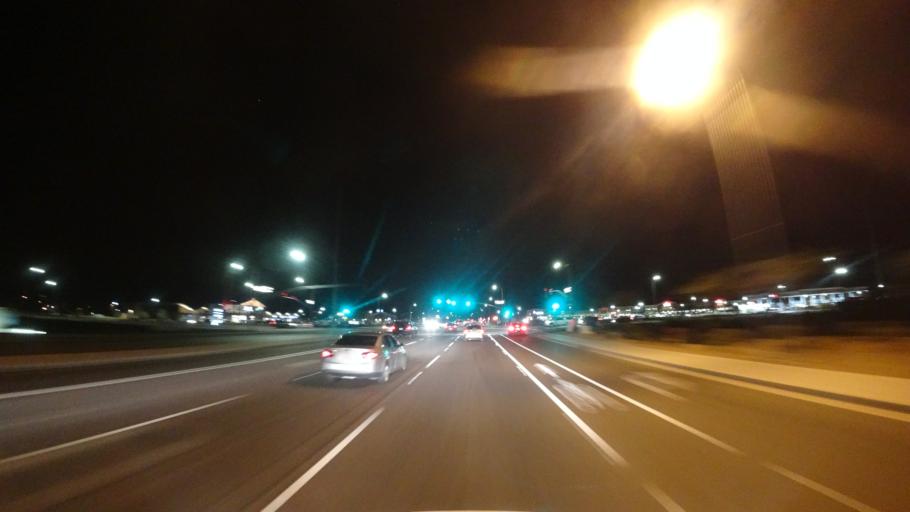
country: US
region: Arizona
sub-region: Maricopa County
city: Chandler
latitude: 33.2490
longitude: -111.7896
